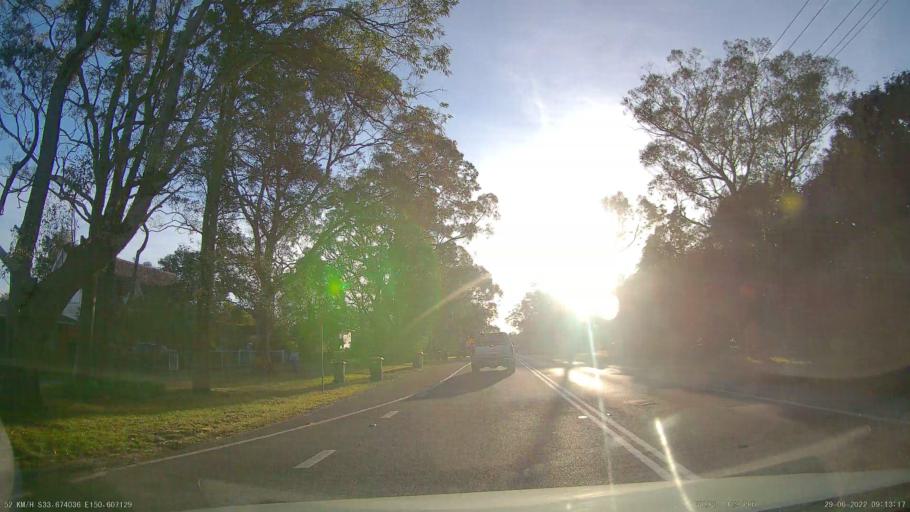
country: AU
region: New South Wales
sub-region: Penrith Municipality
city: Emu Heights
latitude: -33.6741
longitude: 150.6071
